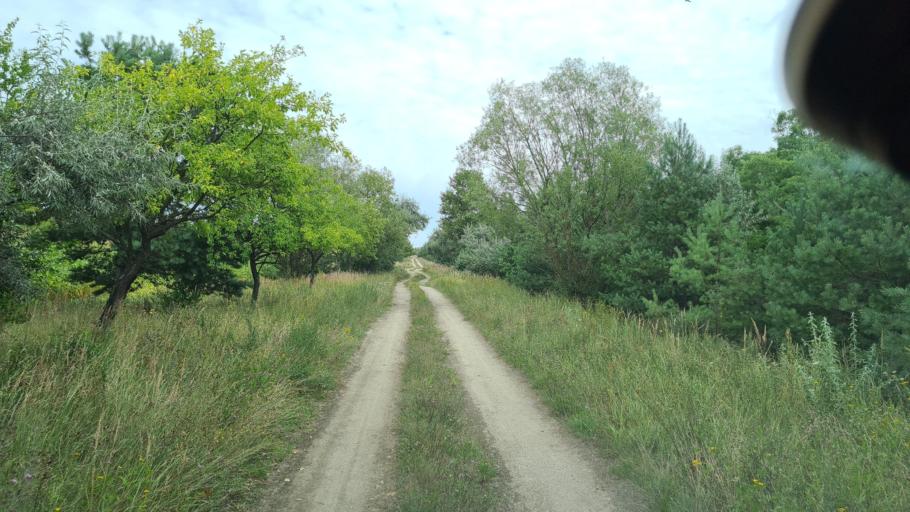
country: DE
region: Brandenburg
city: Spremberg
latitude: 51.5764
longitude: 14.3000
